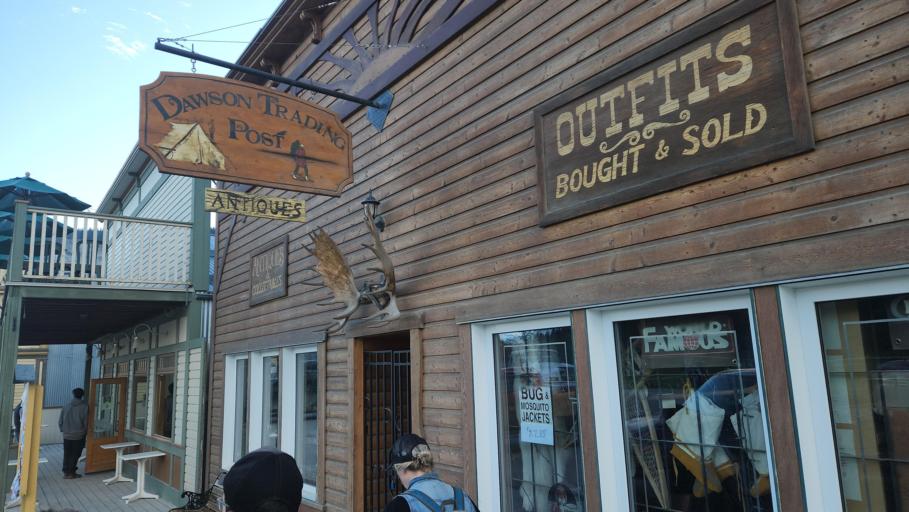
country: CA
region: Yukon
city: Dawson City
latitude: 64.0620
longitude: -139.4359
